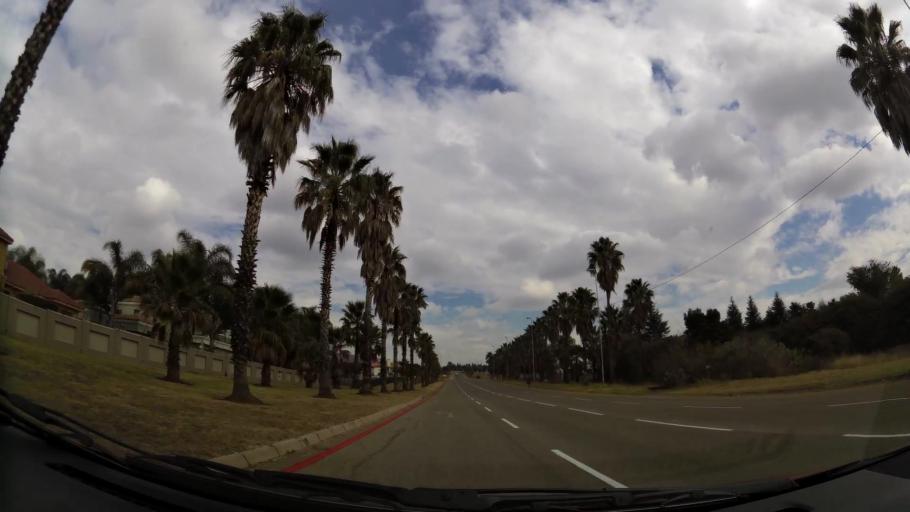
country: ZA
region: Gauteng
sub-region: West Rand District Municipality
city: Muldersdriseloop
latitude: -26.0763
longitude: 27.8623
